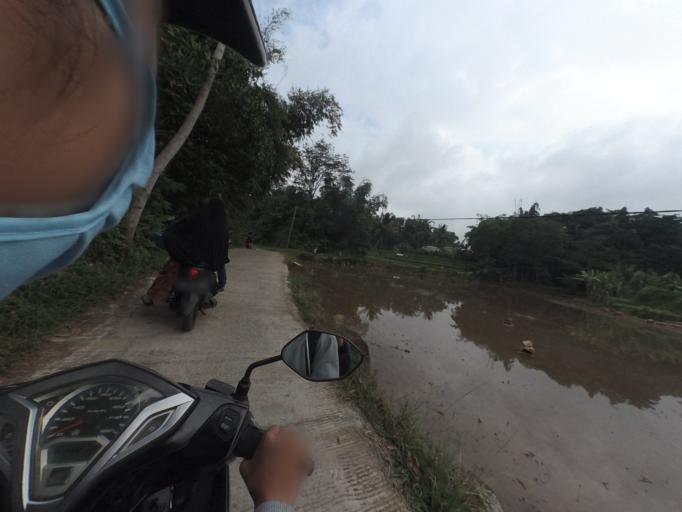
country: ID
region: West Java
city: Ciampea
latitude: -6.6873
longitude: 106.6528
